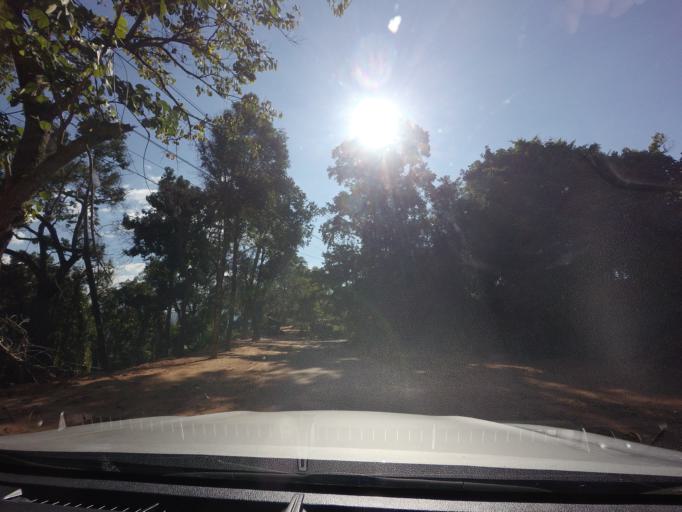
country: TH
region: Lampang
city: Mueang Pan
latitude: 18.8292
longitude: 99.3909
